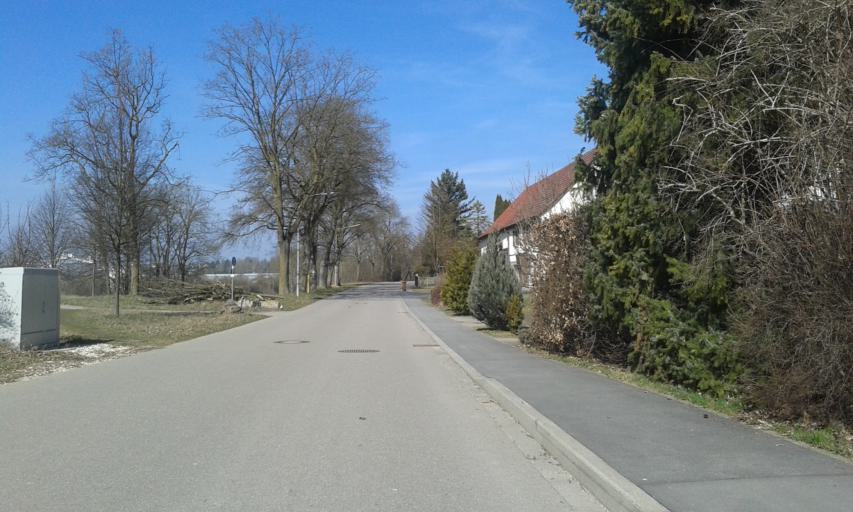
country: DE
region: Baden-Wuerttemberg
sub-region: Tuebingen Region
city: Dettingen
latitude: 48.2648
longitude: 9.7322
